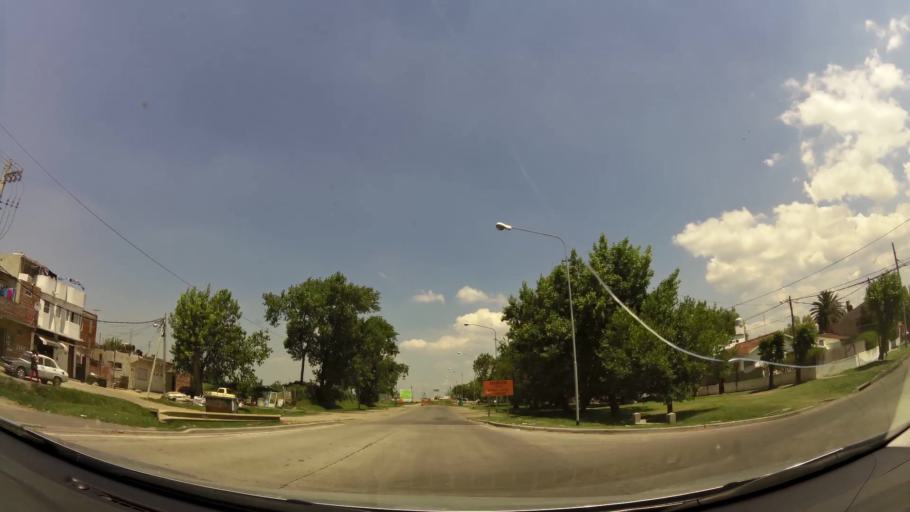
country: AR
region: Buenos Aires
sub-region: Partido de Tigre
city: Tigre
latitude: -34.4460
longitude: -58.5971
